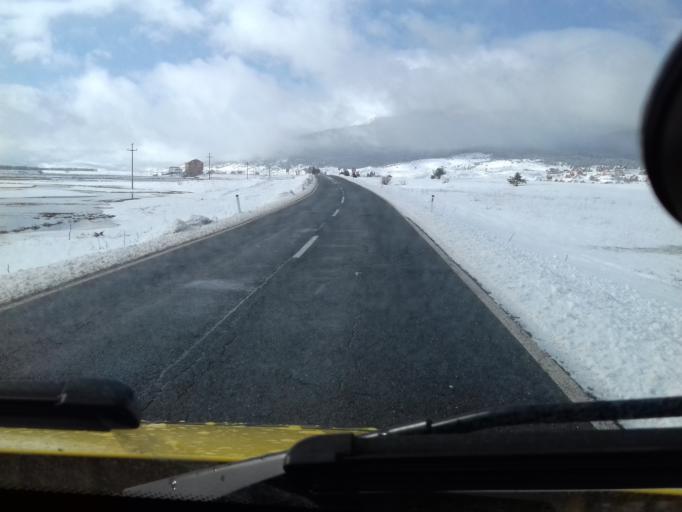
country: BA
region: Federation of Bosnia and Herzegovina
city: Tomislavgrad
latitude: 43.9489
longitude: 17.2197
